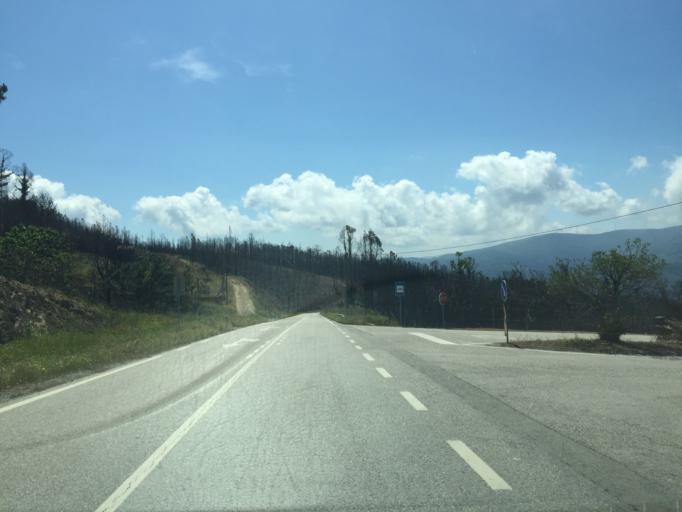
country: PT
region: Coimbra
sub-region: Pampilhosa da Serra
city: Pampilhosa da Serra
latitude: 40.0053
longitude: -7.9786
